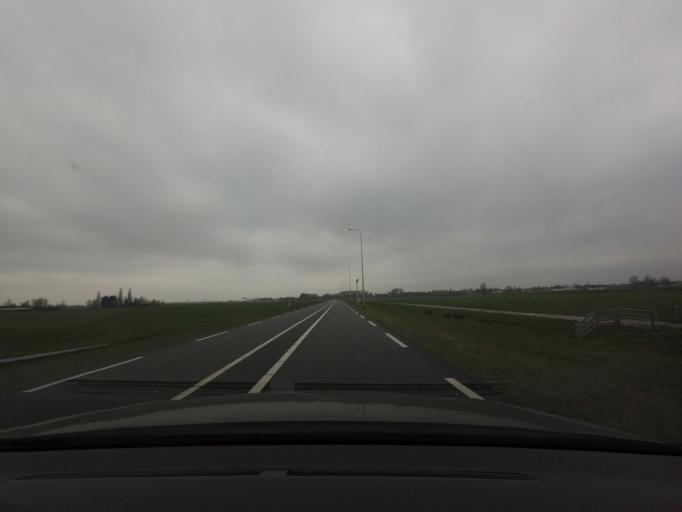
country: NL
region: North Holland
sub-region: Gemeente Uithoorn
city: Uithoorn
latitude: 52.2333
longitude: 4.8484
